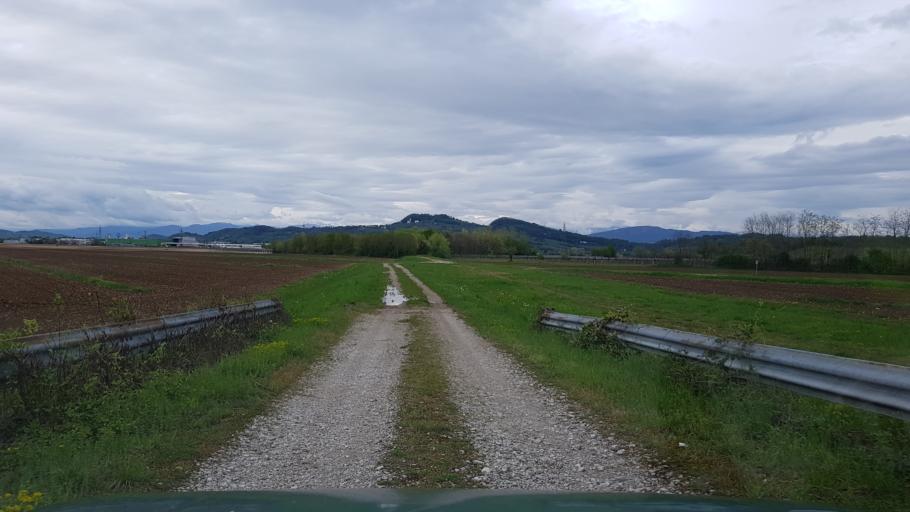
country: IT
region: Friuli Venezia Giulia
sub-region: Provincia di Gorizia
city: Mariano del Friuli
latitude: 45.9317
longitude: 13.4702
